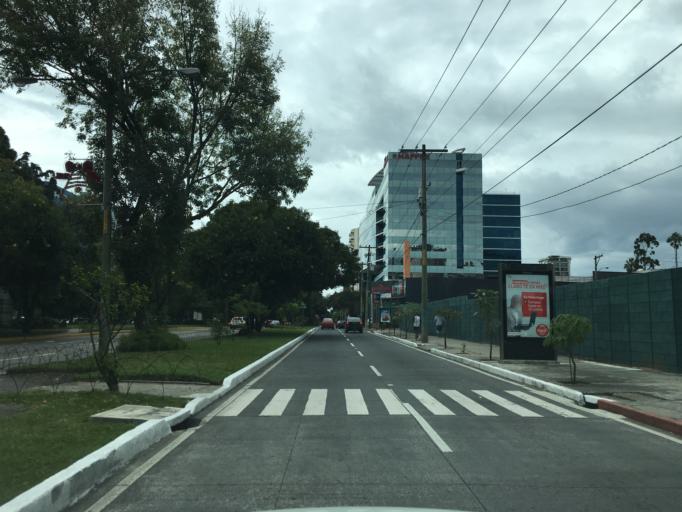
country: GT
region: Guatemala
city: Guatemala City
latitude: 14.6026
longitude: -90.5159
